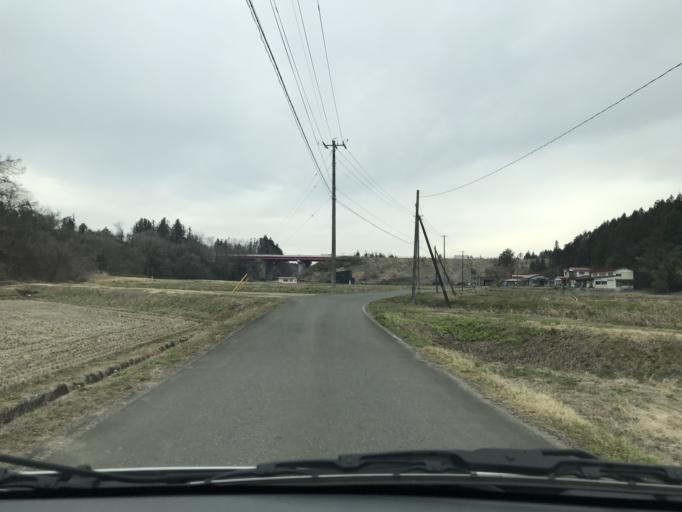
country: JP
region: Iwate
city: Mizusawa
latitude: 39.0925
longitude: 141.1162
